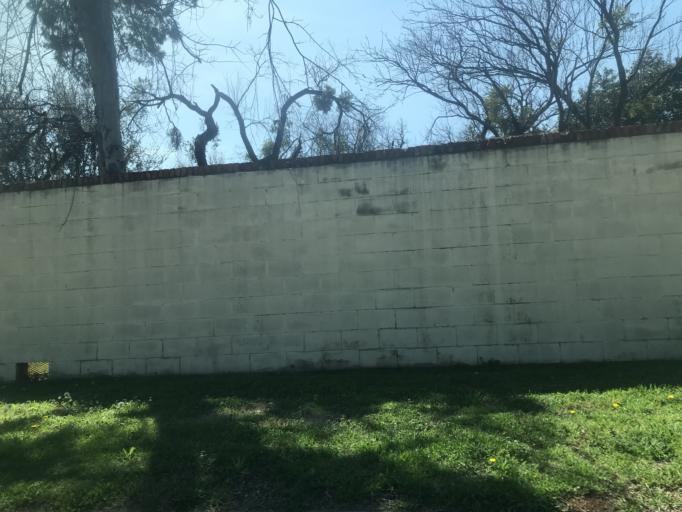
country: US
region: Texas
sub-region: Taylor County
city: Abilene
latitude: 32.4492
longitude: -99.7690
